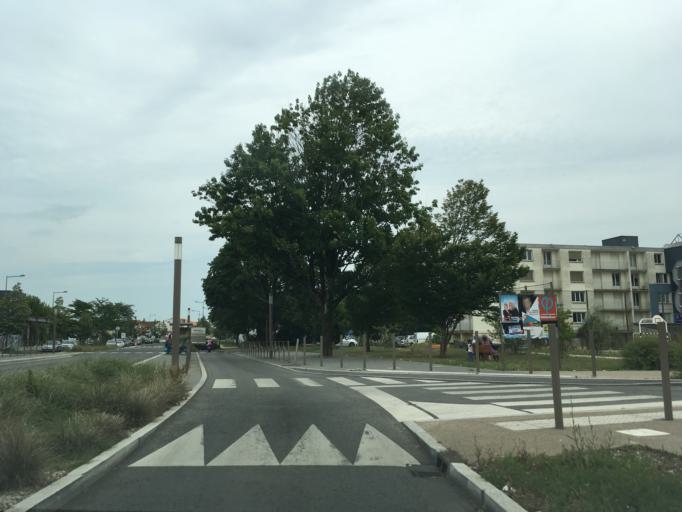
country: FR
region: Poitou-Charentes
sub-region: Departement des Deux-Sevres
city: Niort
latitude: 46.3164
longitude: -0.4784
